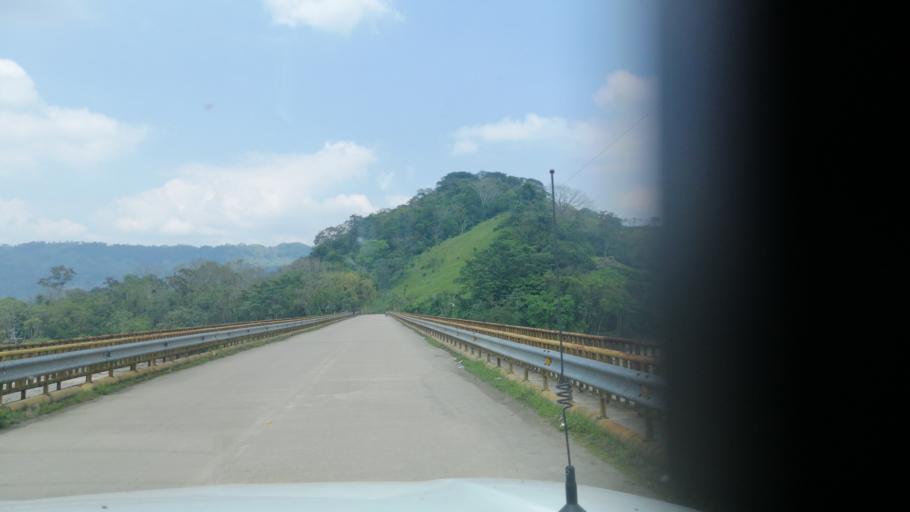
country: MX
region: Chiapas
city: Ostuacan
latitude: 17.4007
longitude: -93.3332
